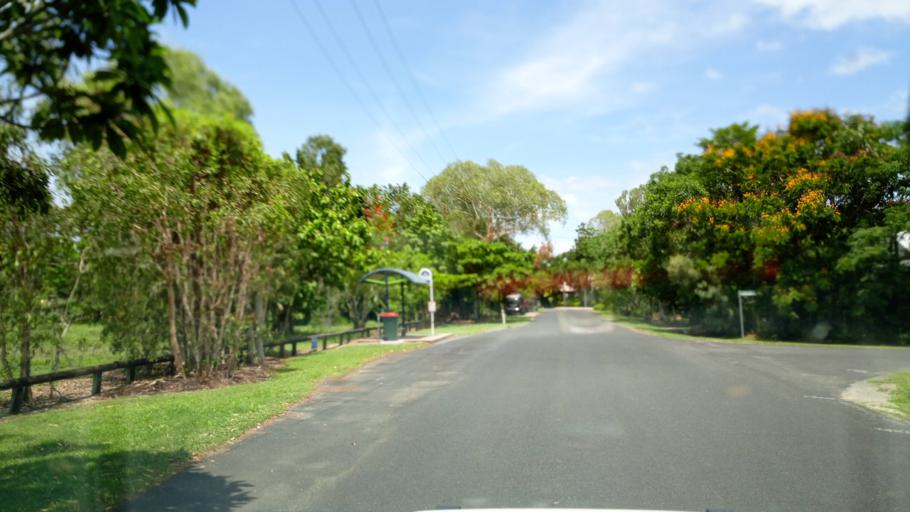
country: AU
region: Queensland
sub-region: Cairns
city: Yorkeys Knob
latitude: -16.8509
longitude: 145.7468
